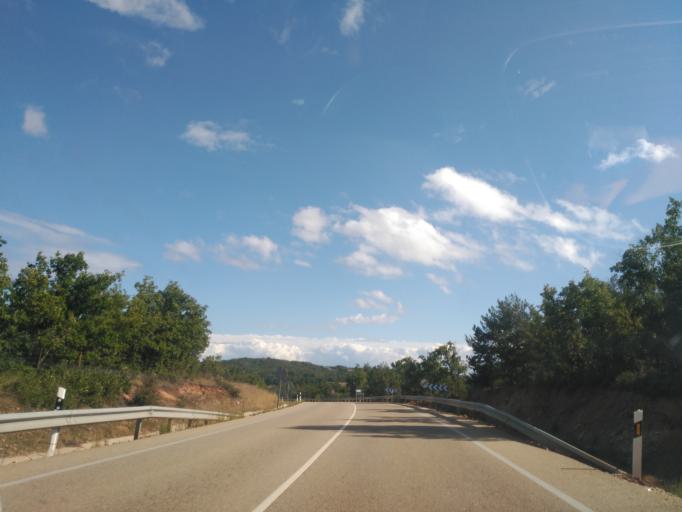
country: ES
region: Castille and Leon
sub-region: Provincia de Burgos
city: Pinilla de los Barruecos
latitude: 41.9407
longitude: -3.2895
